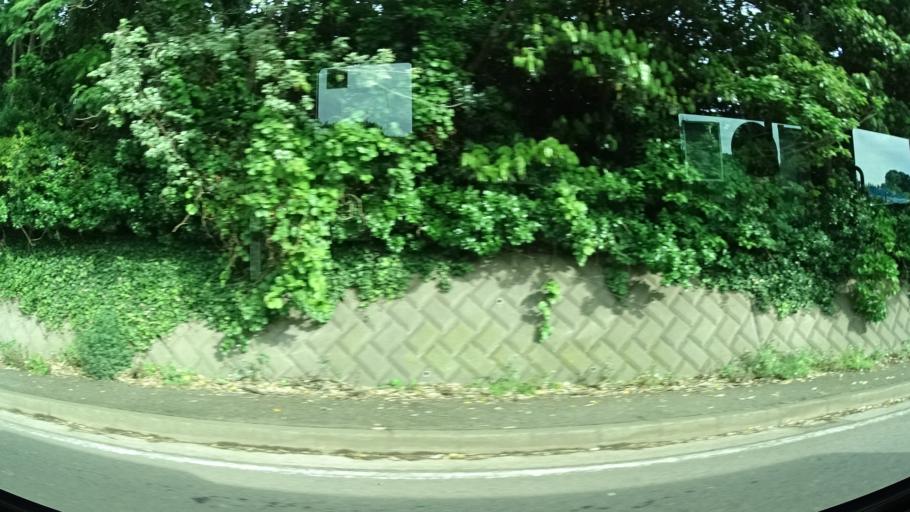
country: JP
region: Kanagawa
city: Miura
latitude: 35.1550
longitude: 139.6703
